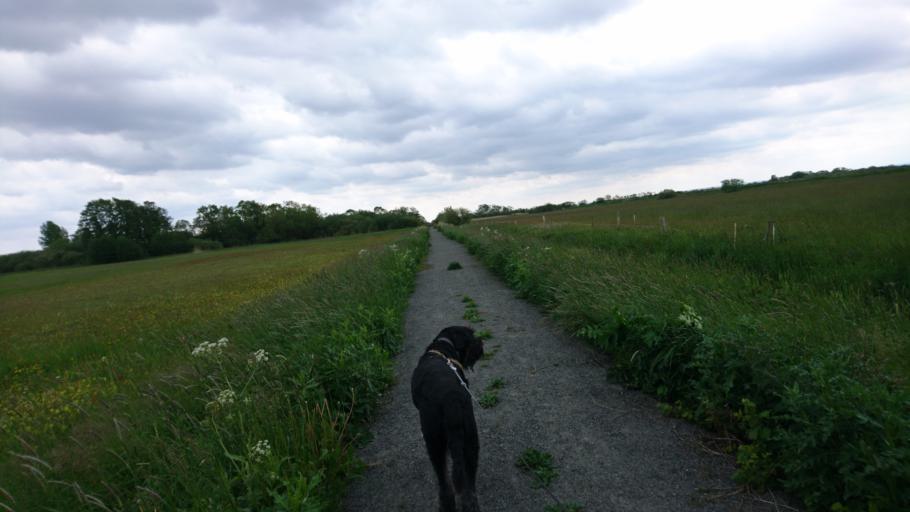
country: SE
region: Skane
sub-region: Kristianstads Kommun
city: Fjalkinge
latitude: 56.0053
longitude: 14.2414
